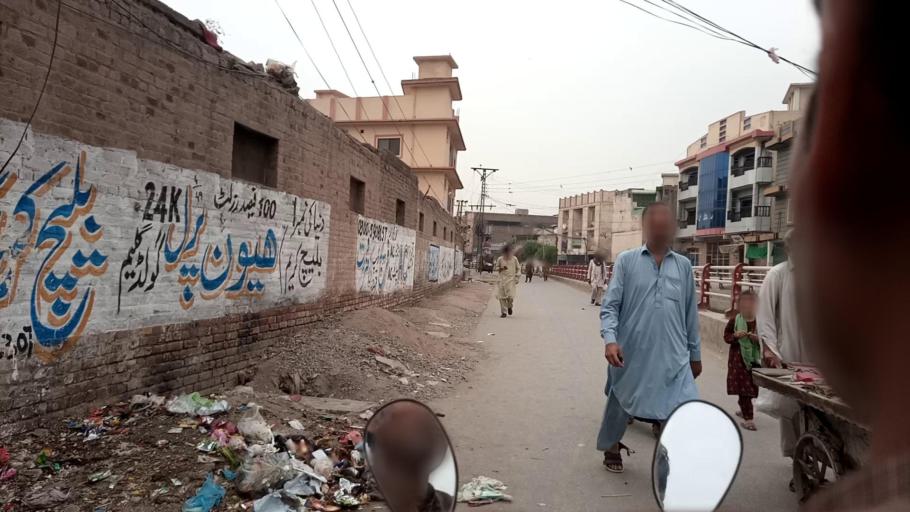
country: PK
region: Khyber Pakhtunkhwa
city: Peshawar
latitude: 34.0207
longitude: 71.5925
